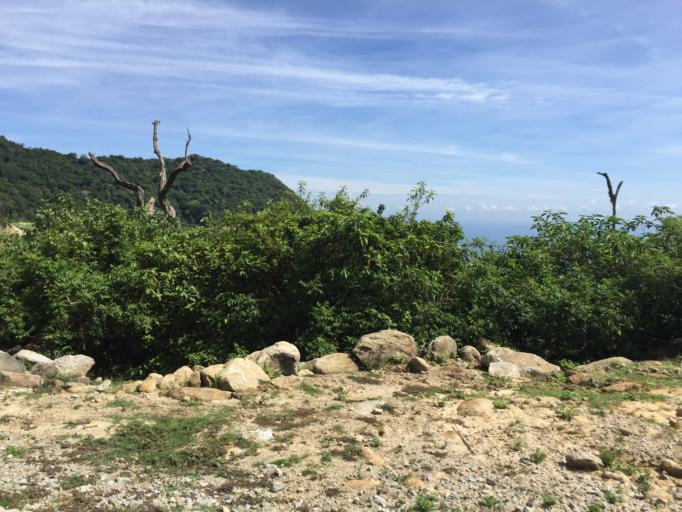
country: VN
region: Quang Nam
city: Hoi An
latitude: 15.9443
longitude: 108.5316
